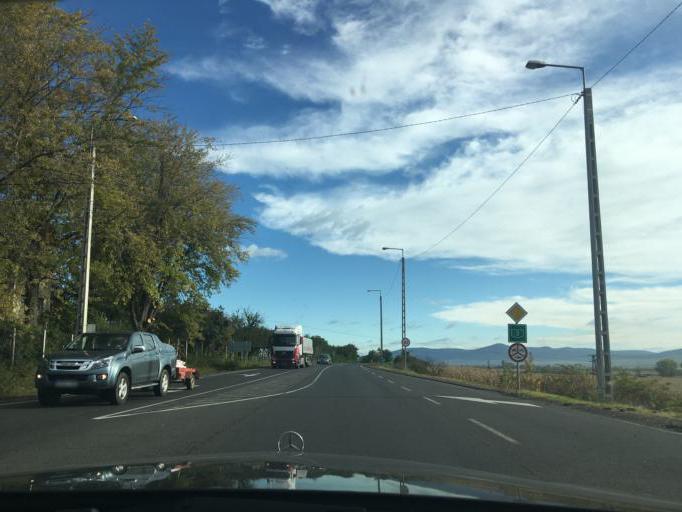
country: HU
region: Borsod-Abauj-Zemplen
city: Encs
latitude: 48.3364
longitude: 21.1072
